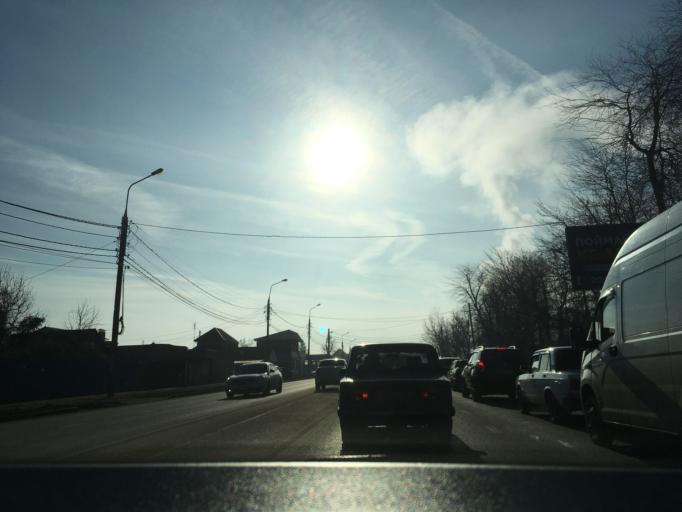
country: RU
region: Krasnodarskiy
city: Krasnodar
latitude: 45.0971
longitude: 39.0134
